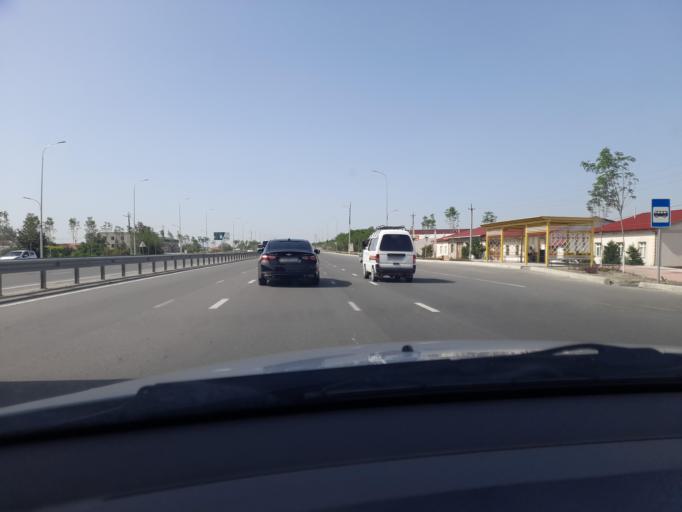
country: UZ
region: Samarqand
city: Daxbet
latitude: 39.7191
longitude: 66.9486
